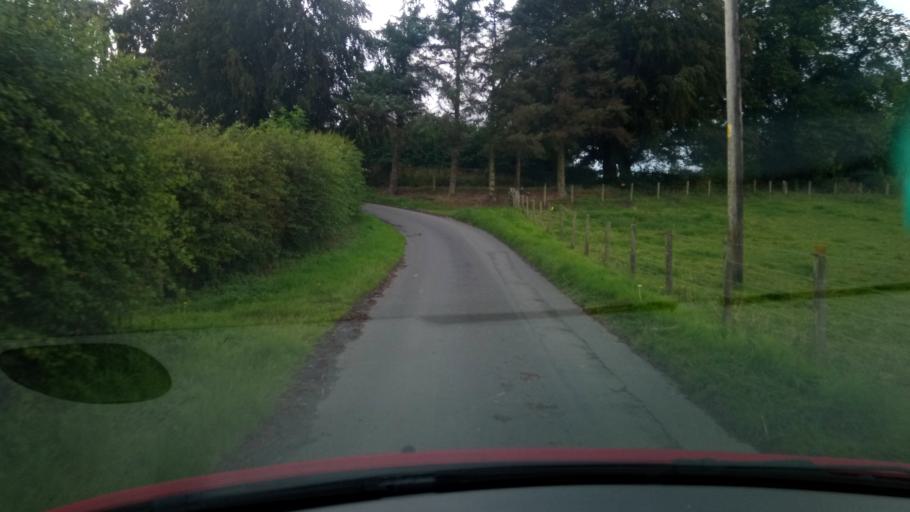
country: GB
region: Scotland
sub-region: The Scottish Borders
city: Hawick
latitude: 55.4258
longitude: -2.7515
